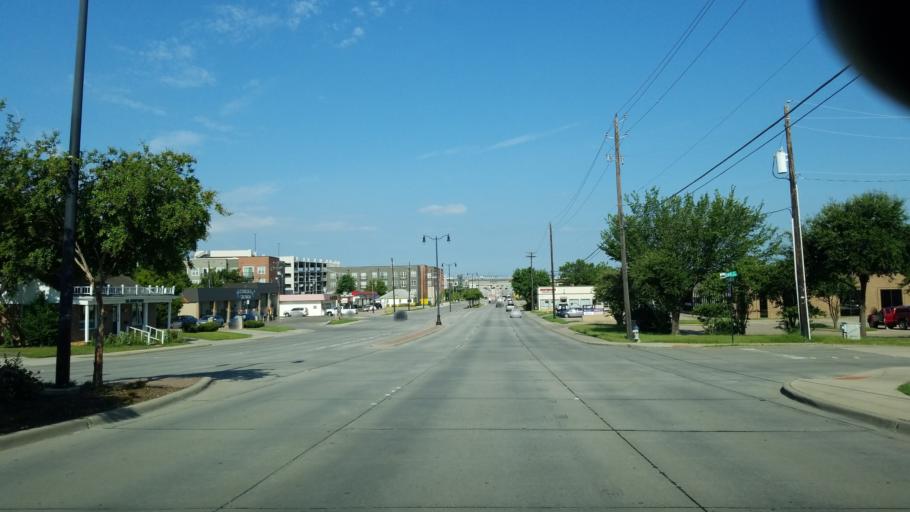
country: US
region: Texas
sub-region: Dallas County
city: Carrollton
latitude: 32.9538
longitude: -96.9028
